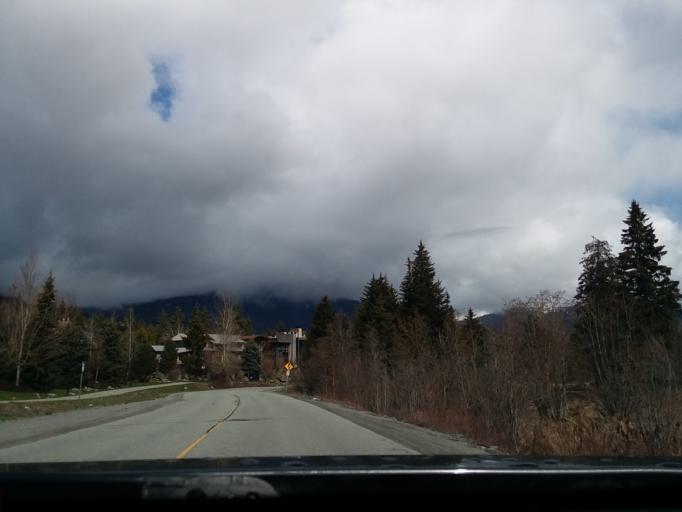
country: CA
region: British Columbia
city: Whistler
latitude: 50.1242
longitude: -122.9546
